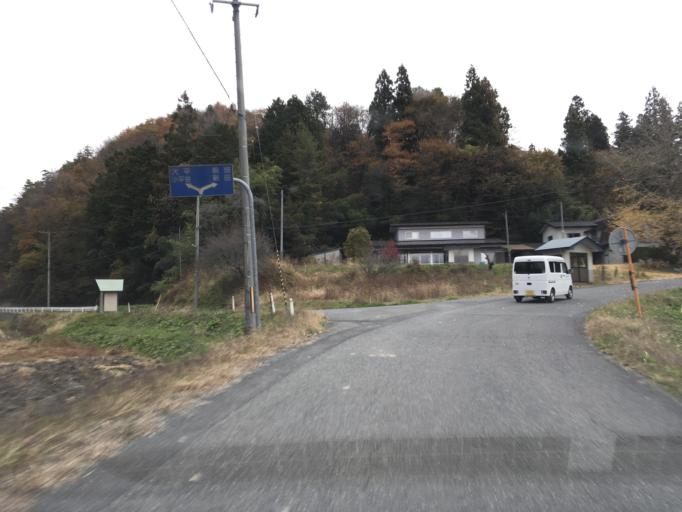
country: JP
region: Iwate
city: Mizusawa
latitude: 39.0481
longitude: 141.3332
